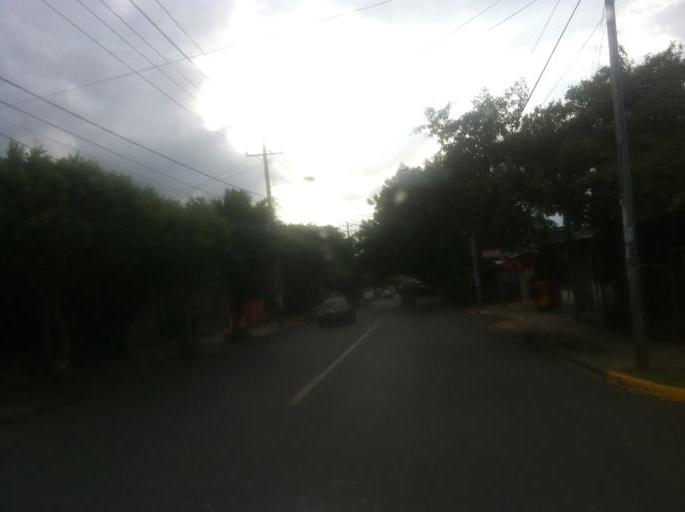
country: NI
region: Managua
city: Managua
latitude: 12.1203
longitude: -86.2418
